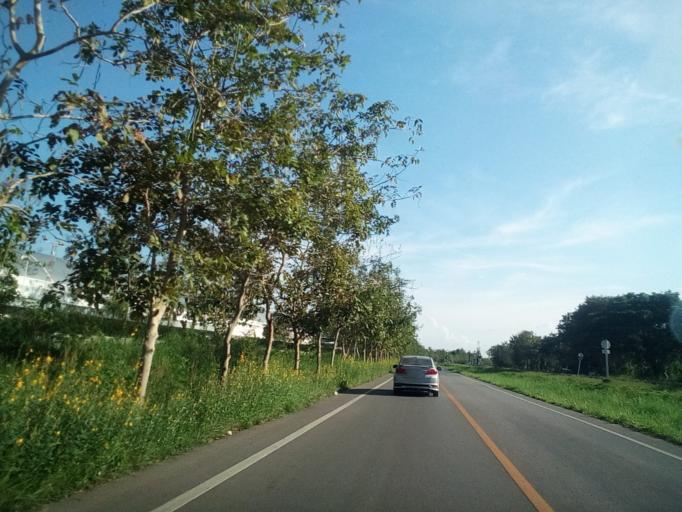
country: TH
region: Chiang Mai
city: Saraphi
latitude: 18.7044
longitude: 99.0444
